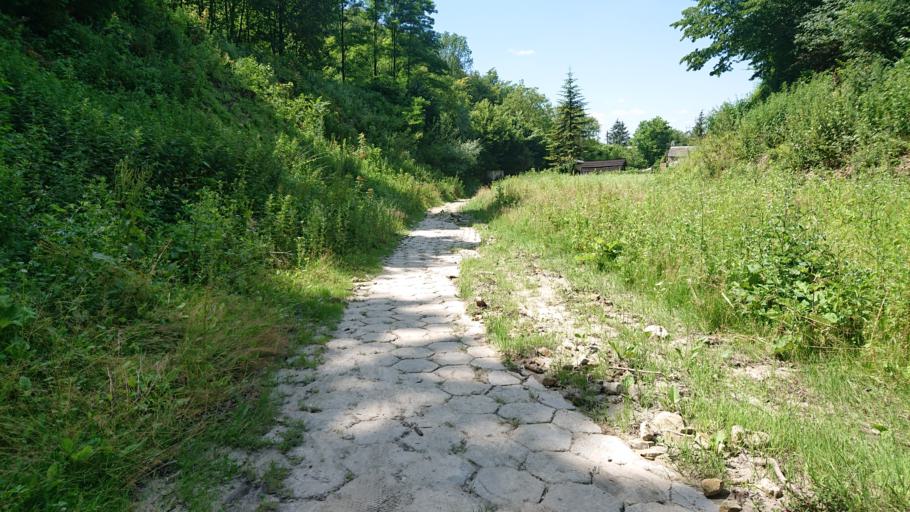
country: PL
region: Lublin Voivodeship
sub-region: Powiat pulawski
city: Kazimierz Dolny
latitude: 51.3285
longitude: 21.9598
